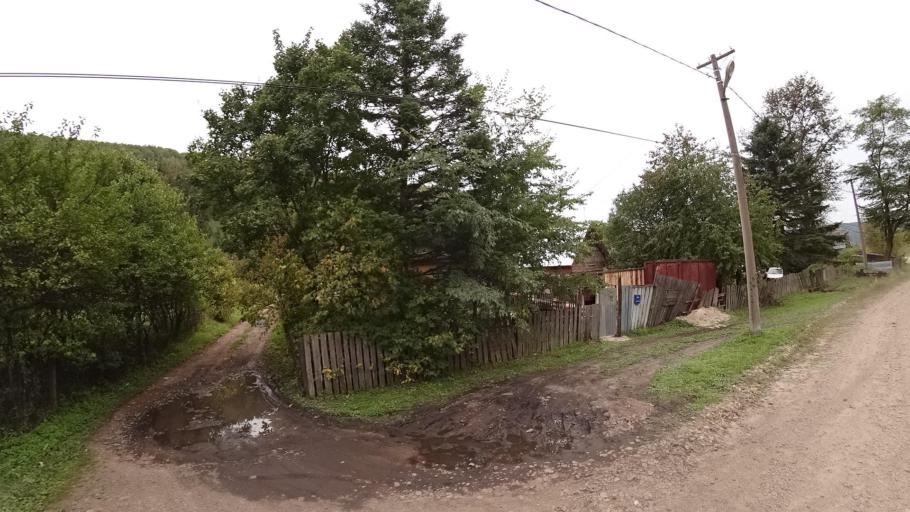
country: RU
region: Jewish Autonomous Oblast
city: Khingansk
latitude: 49.0271
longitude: 131.0756
